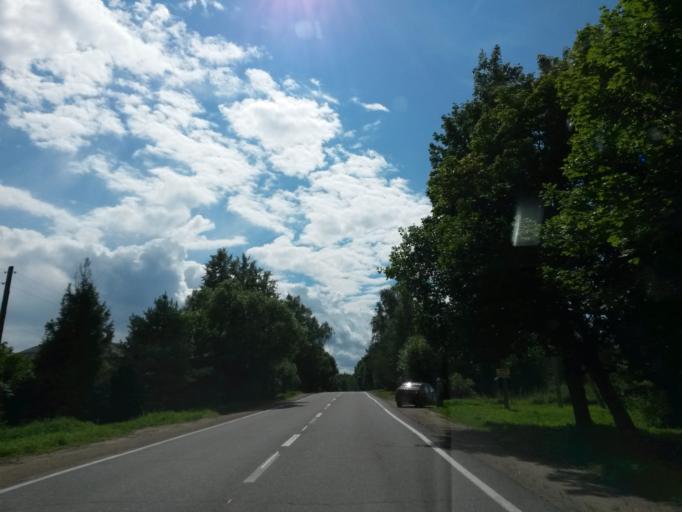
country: RU
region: Jaroslavl
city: Gavrilov-Yam
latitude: 57.2824
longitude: 39.9535
